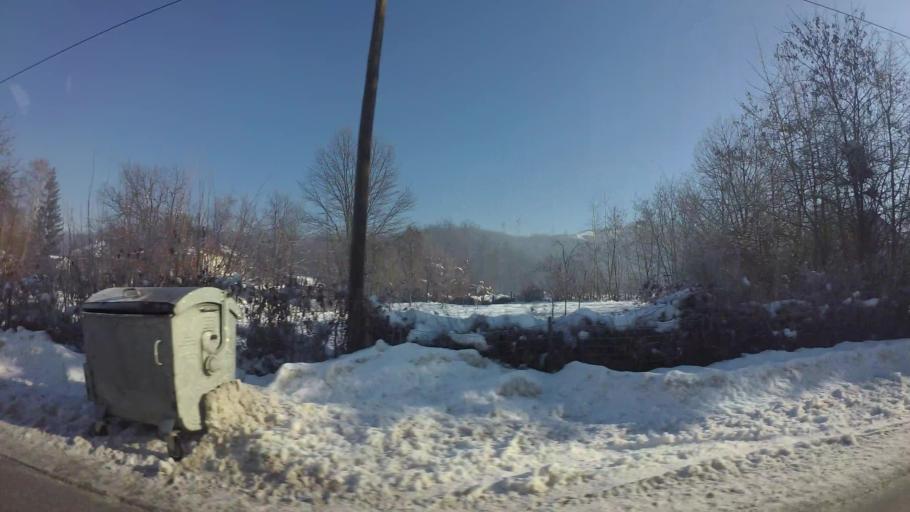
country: BA
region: Federation of Bosnia and Herzegovina
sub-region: Kanton Sarajevo
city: Sarajevo
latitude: 43.8185
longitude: 18.3822
